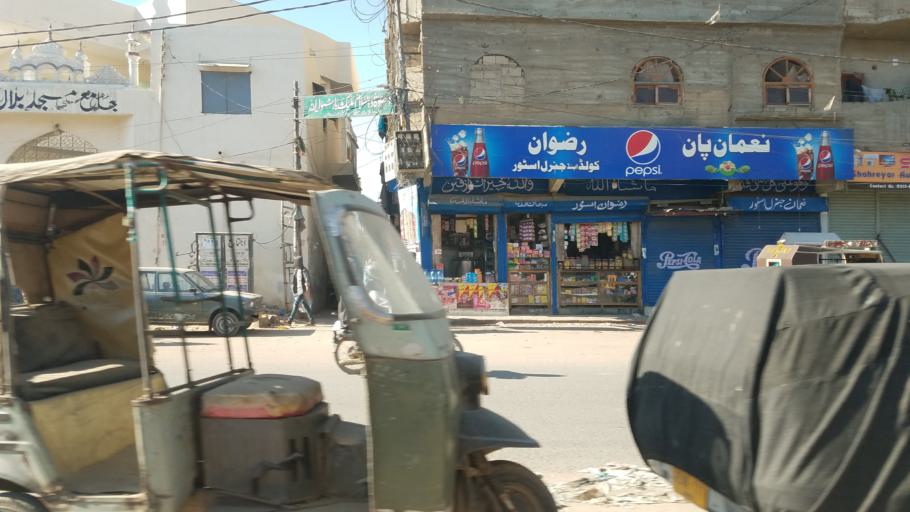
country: PK
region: Sindh
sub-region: Karachi District
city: Karachi
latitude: 24.9209
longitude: 67.0514
